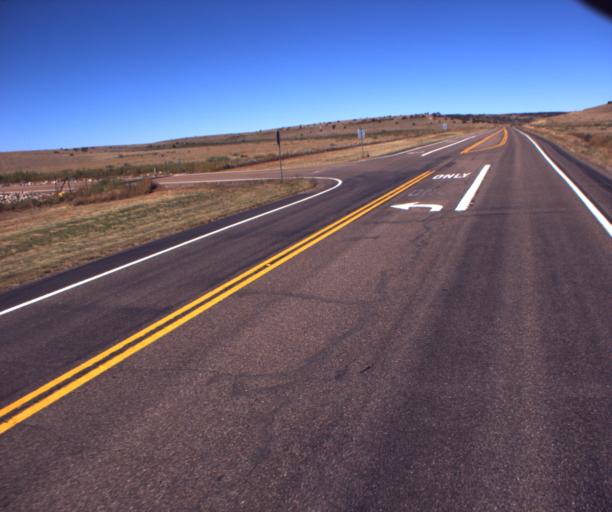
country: US
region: Arizona
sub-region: Apache County
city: Saint Johns
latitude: 34.3222
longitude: -109.3839
